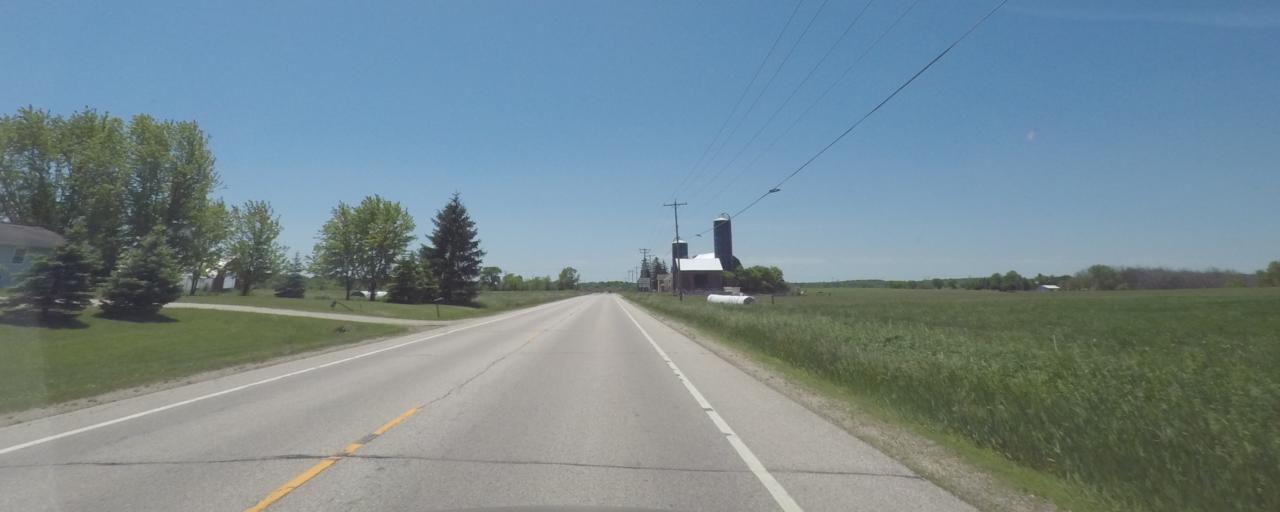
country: US
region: Wisconsin
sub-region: Ozaukee County
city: Kohler
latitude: 43.5603
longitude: -88.0720
